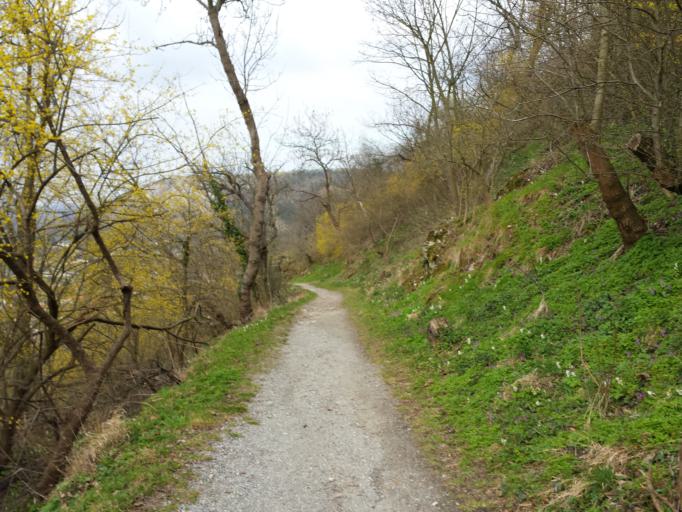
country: AT
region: Lower Austria
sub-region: Politischer Bezirk Bruck an der Leitha
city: Hainburg an der Donau
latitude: 48.1427
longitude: 16.9469
